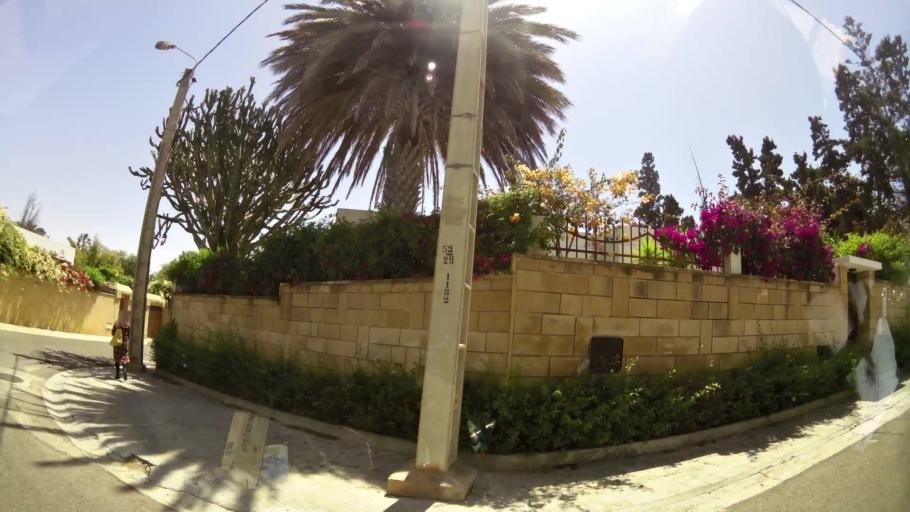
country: MA
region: Souss-Massa-Draa
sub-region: Agadir-Ida-ou-Tnan
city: Agadir
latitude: 30.4298
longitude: -9.5981
